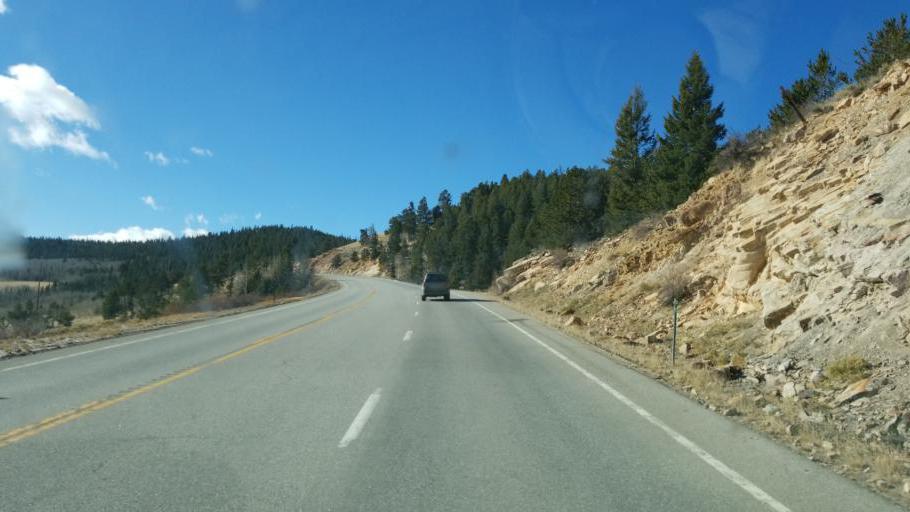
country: US
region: Colorado
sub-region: Park County
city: Fairplay
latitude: 39.2680
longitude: -105.9562
